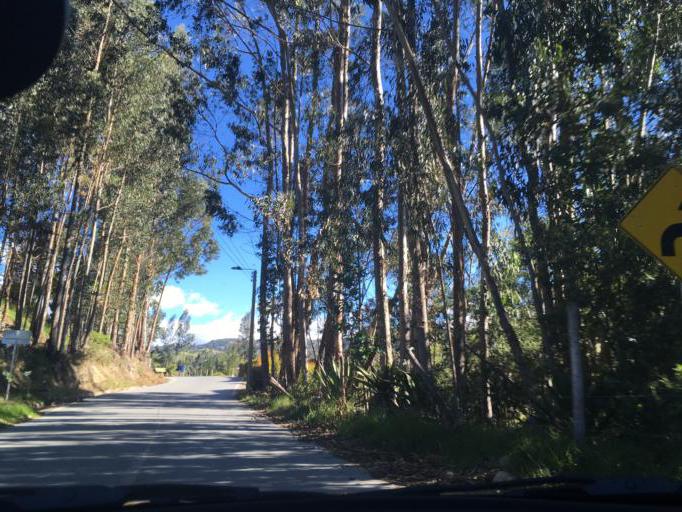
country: CO
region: Boyaca
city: Firavitoba
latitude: 5.5926
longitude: -72.9785
